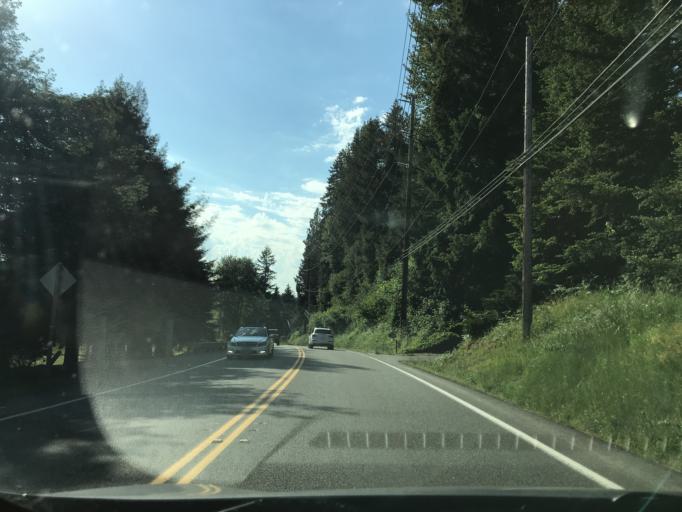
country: US
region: Washington
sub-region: King County
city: Mirrormont
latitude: 47.4536
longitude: -121.9958
